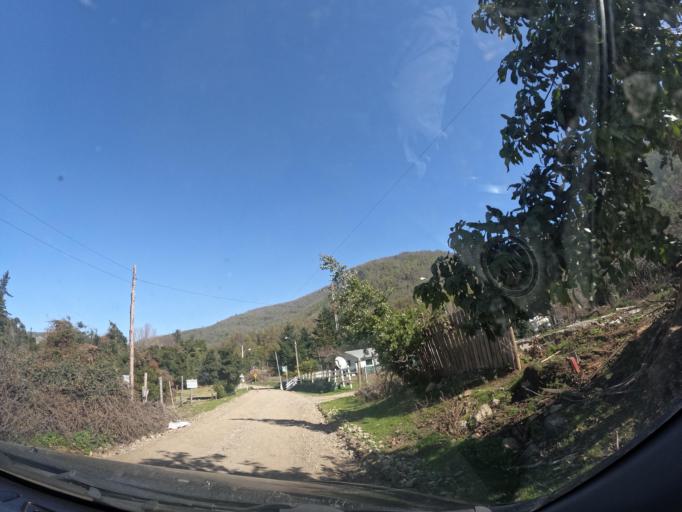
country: CL
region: Maule
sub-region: Provincia de Linares
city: Longavi
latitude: -36.2872
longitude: -71.4159
